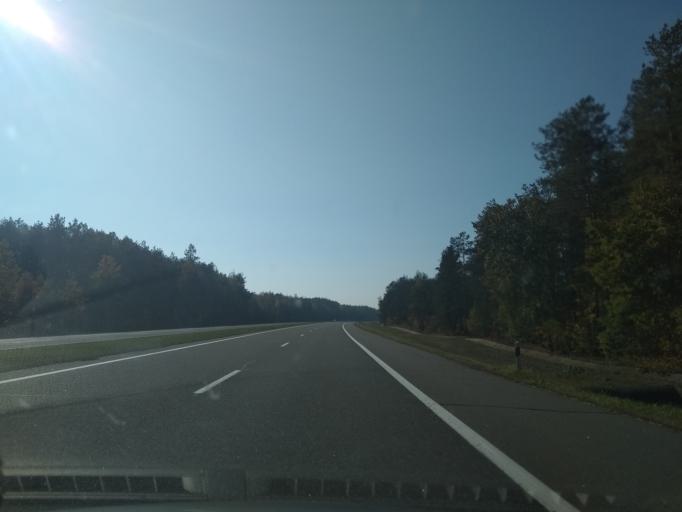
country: BY
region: Brest
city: Antopal'
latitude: 52.3679
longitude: 24.7378
